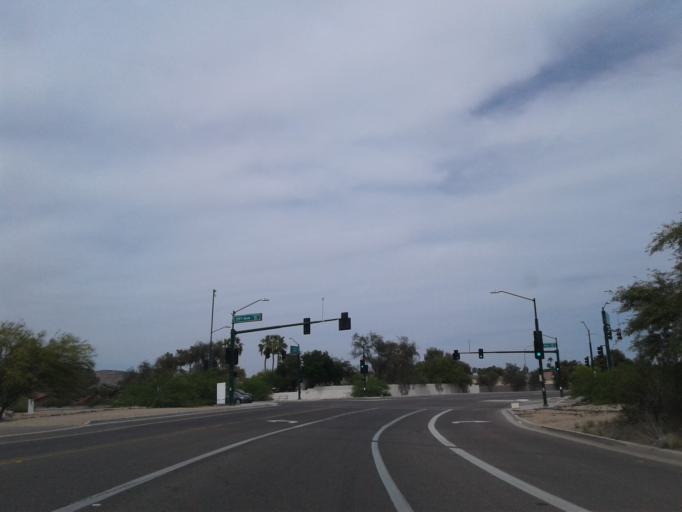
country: US
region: Arizona
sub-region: Maricopa County
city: Peoria
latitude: 33.6974
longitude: -112.1792
